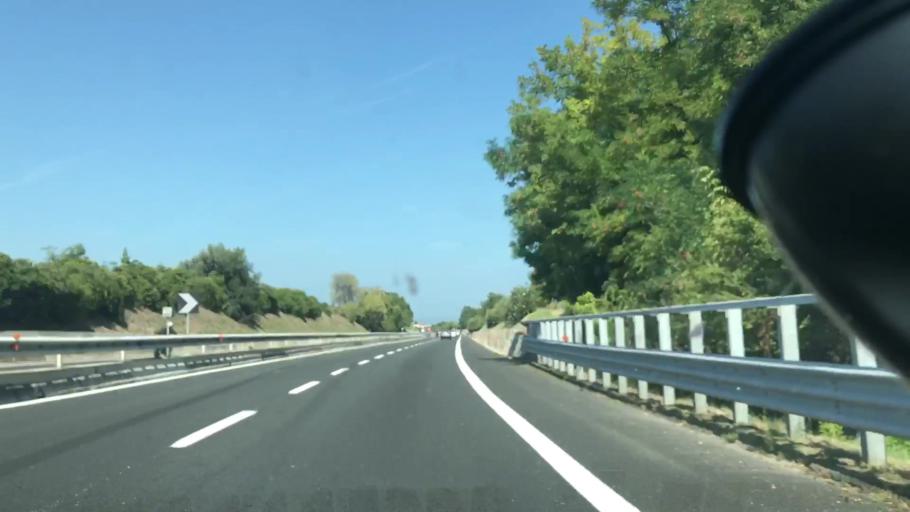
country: IT
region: Abruzzo
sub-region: Provincia di Chieti
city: Ortona
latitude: 42.3405
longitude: 14.3584
